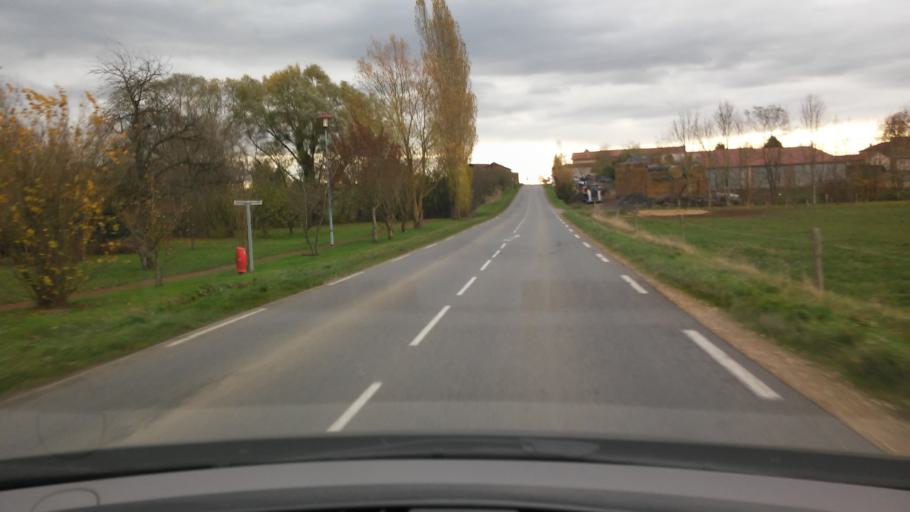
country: FR
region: Lorraine
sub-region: Departement de la Moselle
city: Retonfey
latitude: 49.1624
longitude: 6.3033
